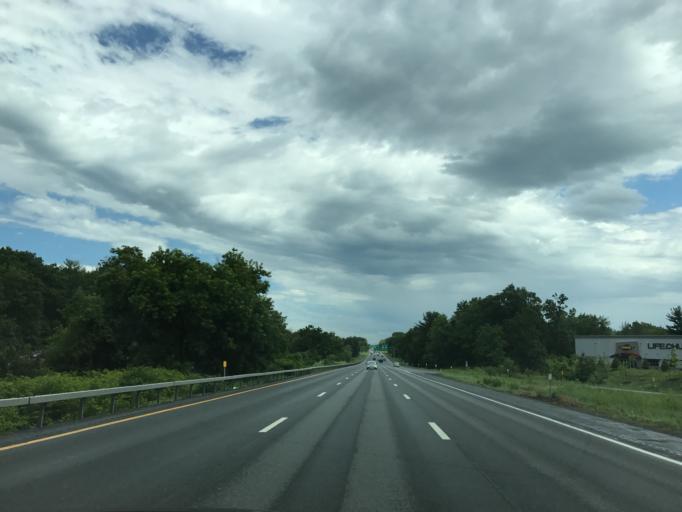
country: US
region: New York
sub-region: Albany County
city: Roessleville
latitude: 42.7406
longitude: -73.7807
